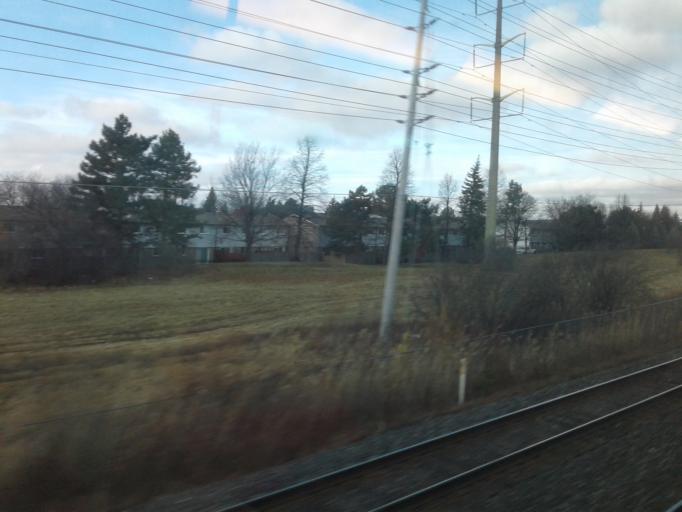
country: CA
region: Ontario
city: Oakville
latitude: 43.5044
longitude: -79.6426
